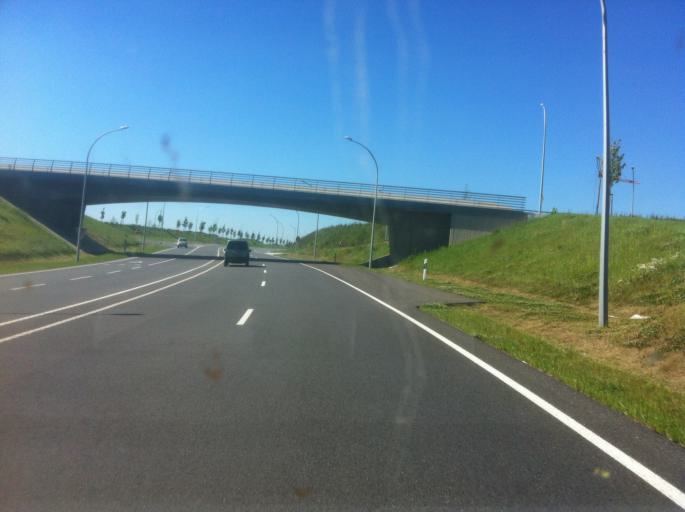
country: LU
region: Grevenmacher
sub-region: Canton de Grevenmacher
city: Junglinster
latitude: 49.7181
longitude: 6.2706
